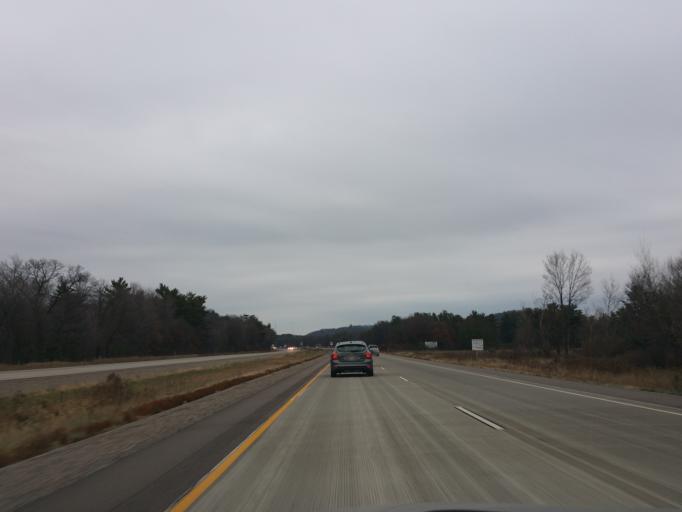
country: US
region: Wisconsin
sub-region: Jackson County
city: Black River Falls
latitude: 44.3575
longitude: -90.9564
